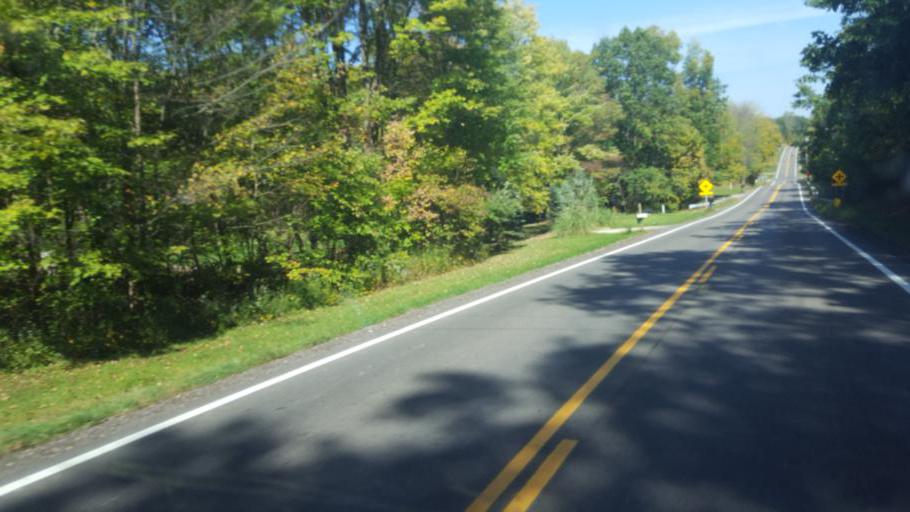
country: US
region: Ohio
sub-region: Richland County
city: Ontario
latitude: 40.7330
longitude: -82.6658
